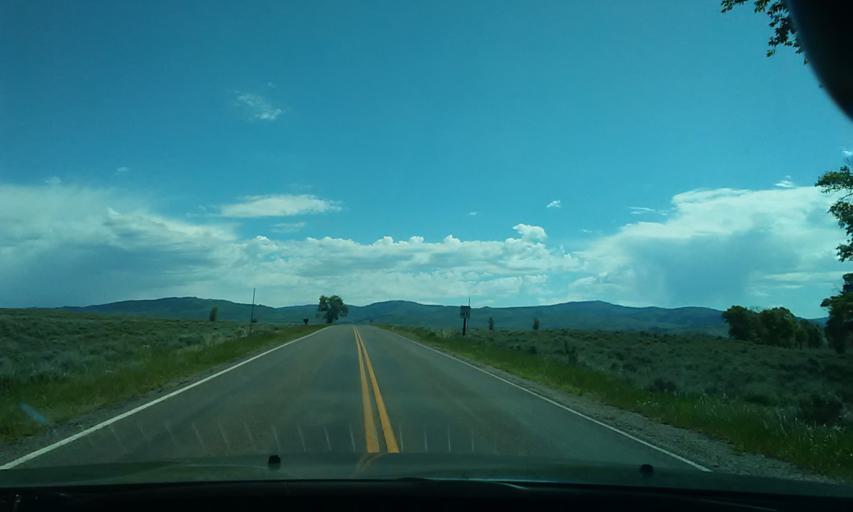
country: US
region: Wyoming
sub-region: Teton County
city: Jackson
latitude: 43.6221
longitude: -110.6680
